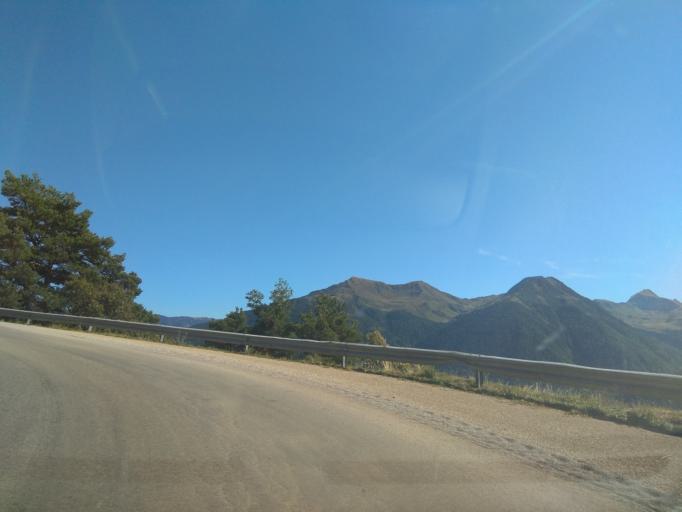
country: ES
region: Catalonia
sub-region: Provincia de Lleida
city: Les
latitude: 42.7501
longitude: 0.7166
